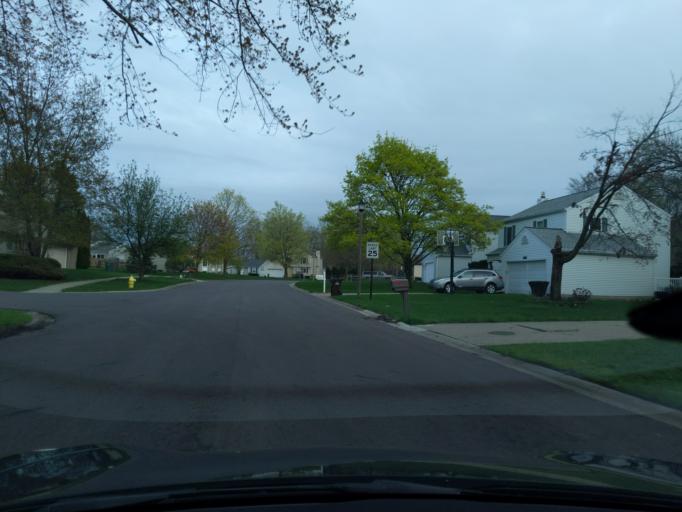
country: US
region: Michigan
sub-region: Eaton County
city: Waverly
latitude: 42.7282
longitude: -84.6145
